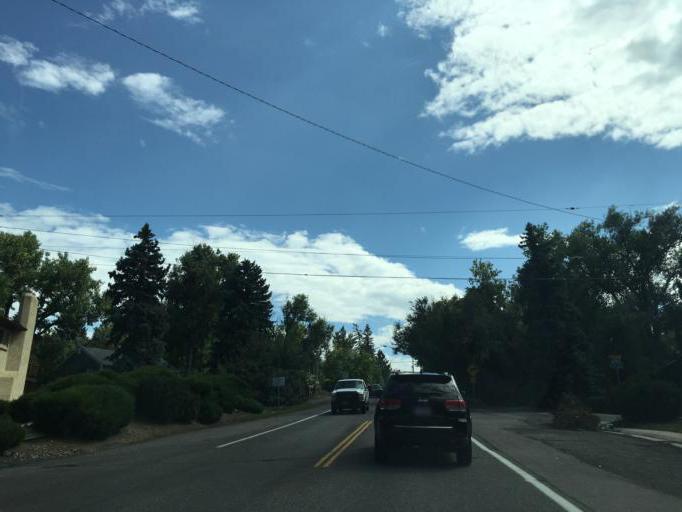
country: US
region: Colorado
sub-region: Jefferson County
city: Applewood
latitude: 39.7427
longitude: -105.1424
